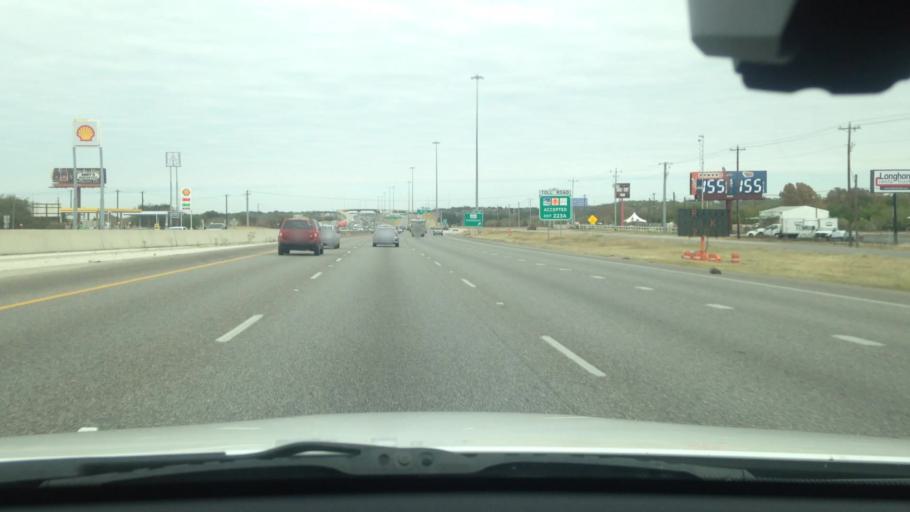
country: US
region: Texas
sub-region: Hays County
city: Buda
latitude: 30.0926
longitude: -97.8164
